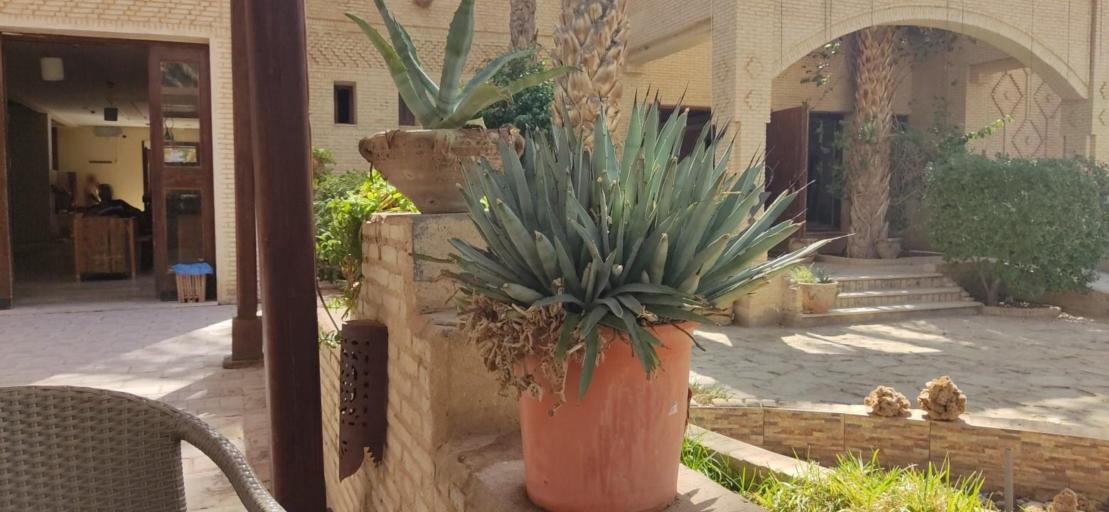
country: TN
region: Tawzar
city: Tozeur
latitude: 33.9173
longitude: 8.1470
